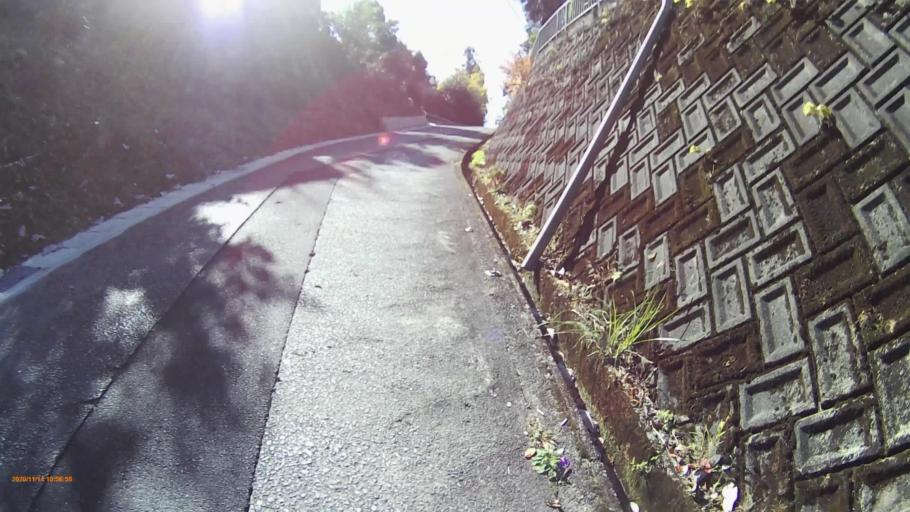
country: JP
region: Gifu
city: Nakatsugawa
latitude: 35.5068
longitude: 137.5183
